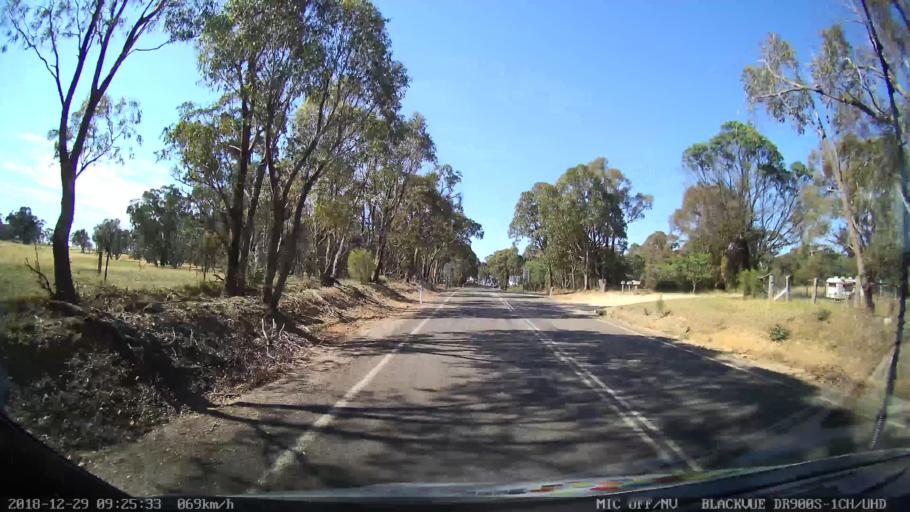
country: AU
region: New South Wales
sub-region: Upper Lachlan Shire
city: Crookwell
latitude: -34.5450
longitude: 149.3940
